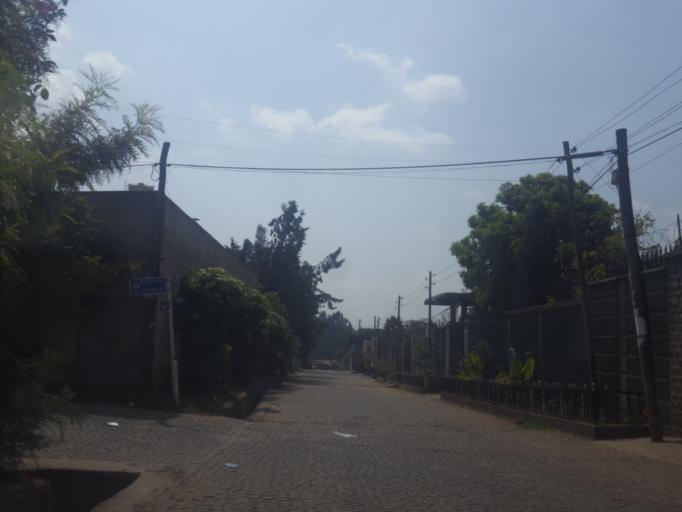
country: ET
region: Adis Abeba
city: Addis Ababa
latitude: 9.0647
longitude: 38.7226
